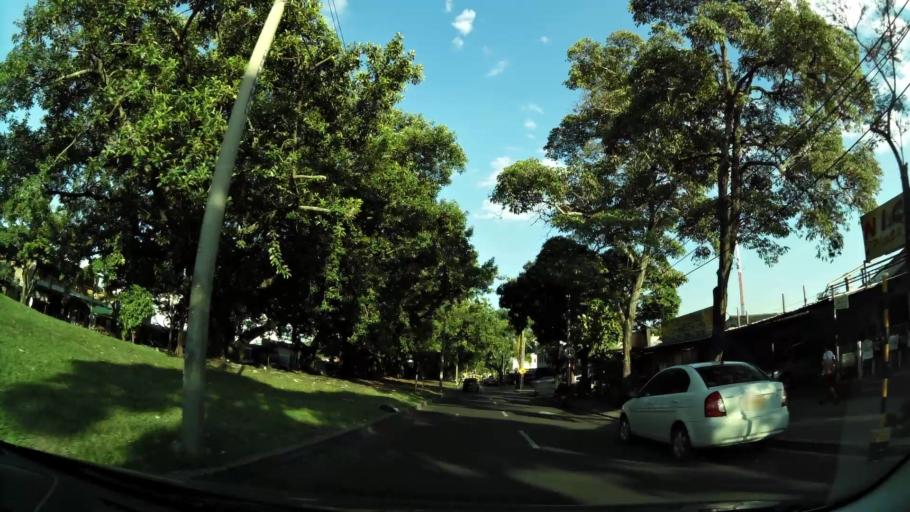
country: CO
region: Valle del Cauca
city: Cali
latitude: 3.4802
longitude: -76.5212
